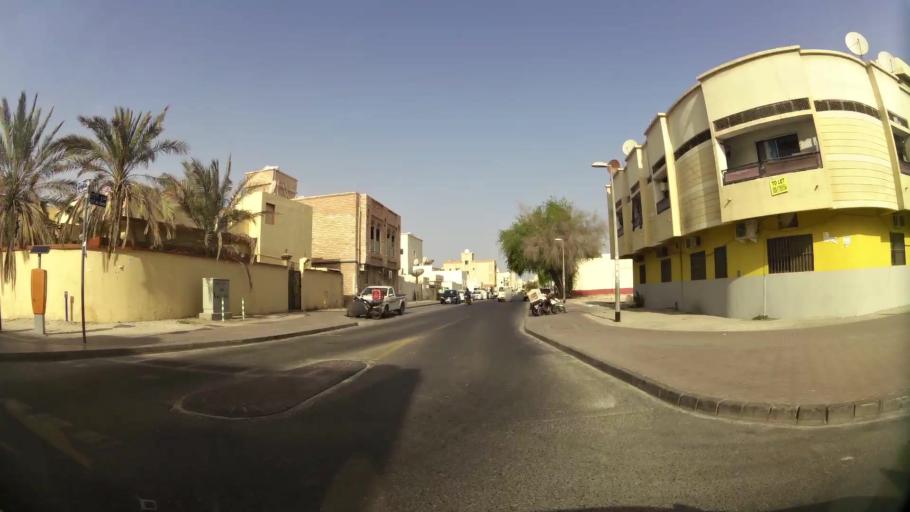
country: AE
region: Ash Shariqah
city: Sharjah
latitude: 25.2772
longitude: 55.3354
